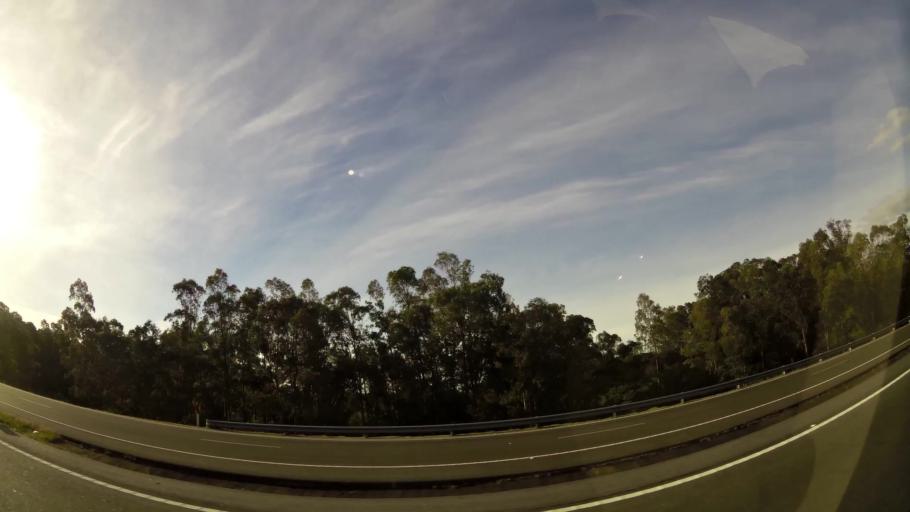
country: UY
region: Maldonado
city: Piriapolis
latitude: -34.7794
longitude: -55.3584
